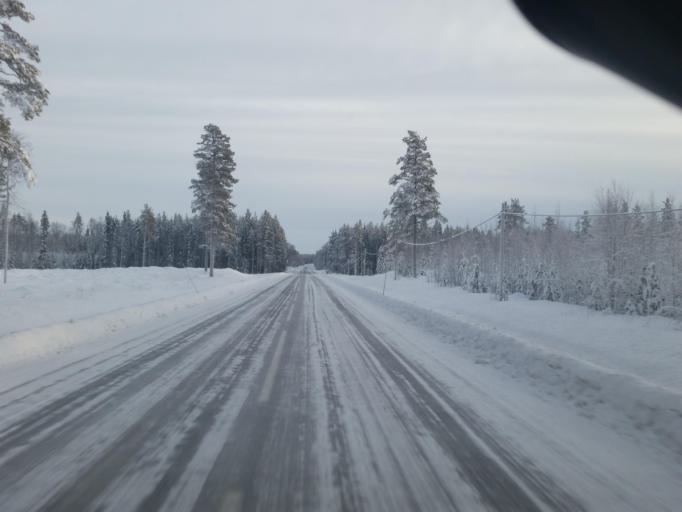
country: SE
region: Norrbotten
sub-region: Pitea Kommun
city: Norrfjarden
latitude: 65.5151
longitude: 21.5415
